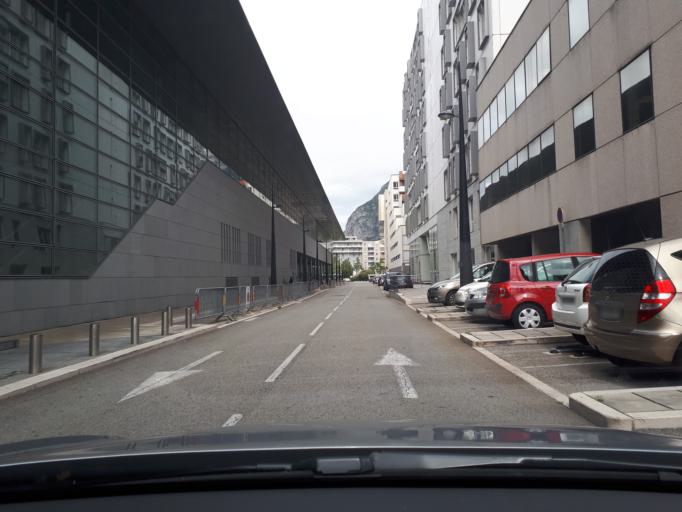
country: FR
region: Rhone-Alpes
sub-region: Departement de l'Isere
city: Saint-Martin-le-Vinoux
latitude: 45.1916
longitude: 5.7118
